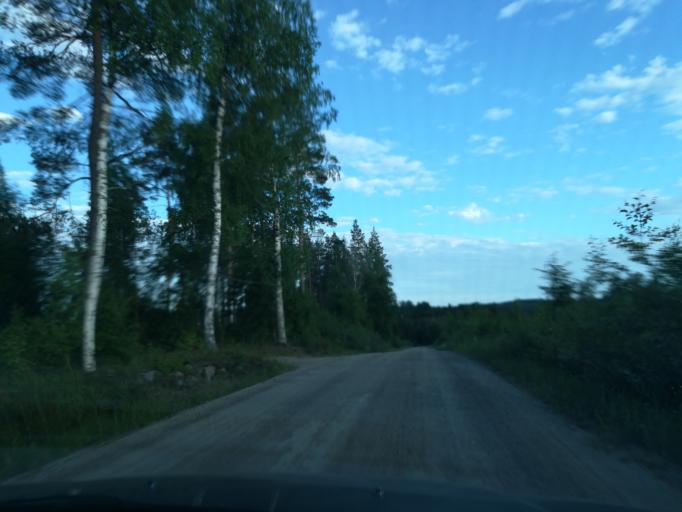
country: FI
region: Southern Savonia
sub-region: Mikkeli
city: Puumala
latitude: 61.6154
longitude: 28.1142
